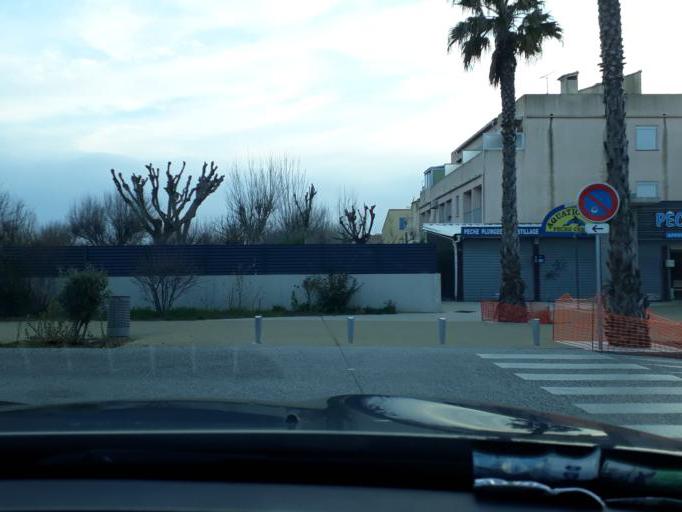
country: FR
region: Languedoc-Roussillon
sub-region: Departement de l'Herault
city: Marseillan
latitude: 43.3157
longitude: 3.5513
